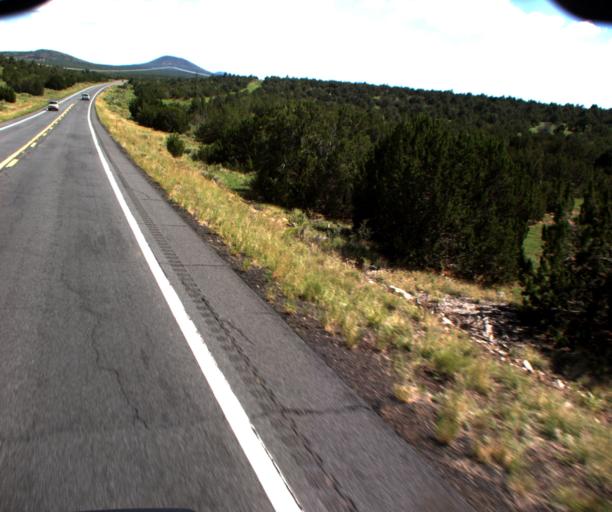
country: US
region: Arizona
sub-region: Coconino County
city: Williams
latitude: 35.4690
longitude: -112.1742
